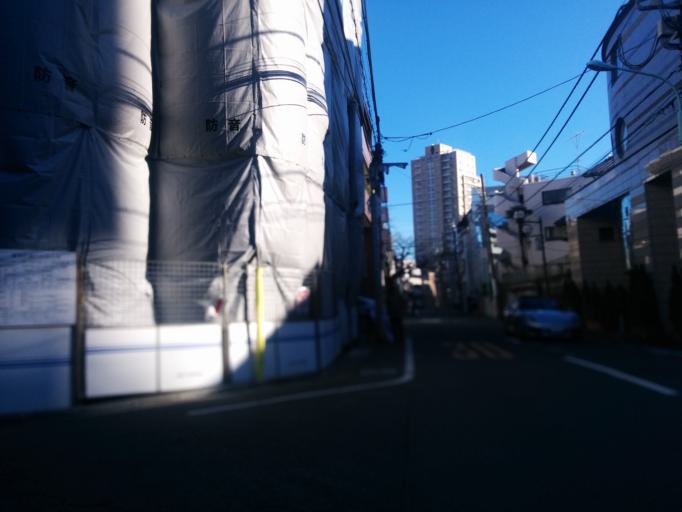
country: JP
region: Tokyo
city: Tokyo
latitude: 35.6764
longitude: 139.7076
